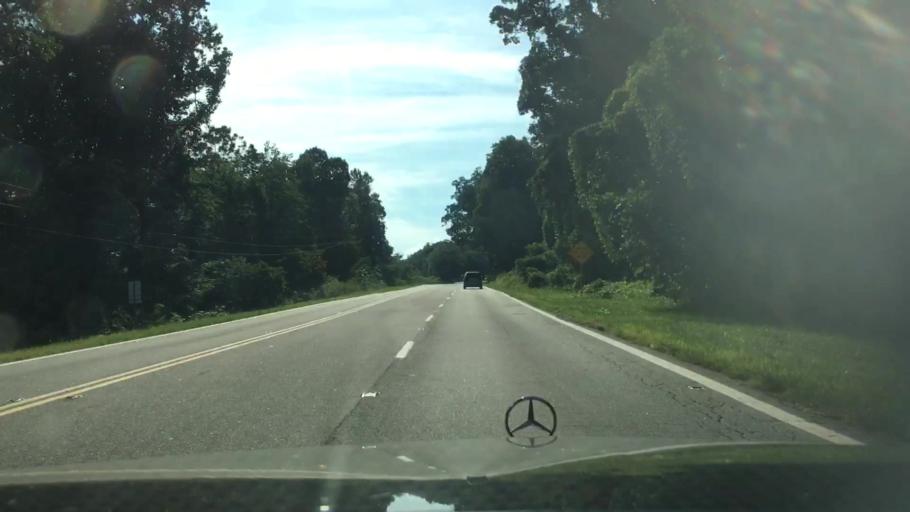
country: US
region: Virginia
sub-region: City of Waynesboro
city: Waynesboro
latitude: 38.0385
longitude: -78.8290
